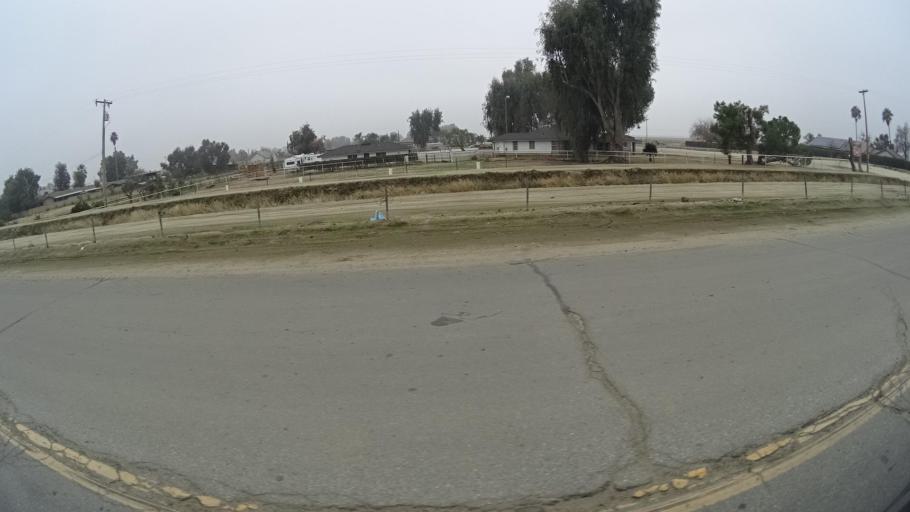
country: US
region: California
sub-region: Kern County
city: Greenfield
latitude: 35.2378
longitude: -119.0199
